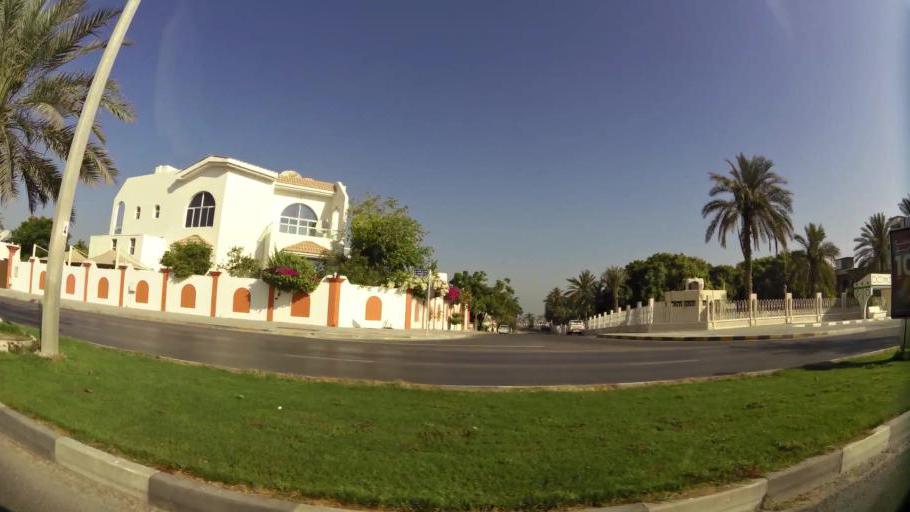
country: AE
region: Ajman
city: Ajman
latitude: 25.3836
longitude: 55.4081
